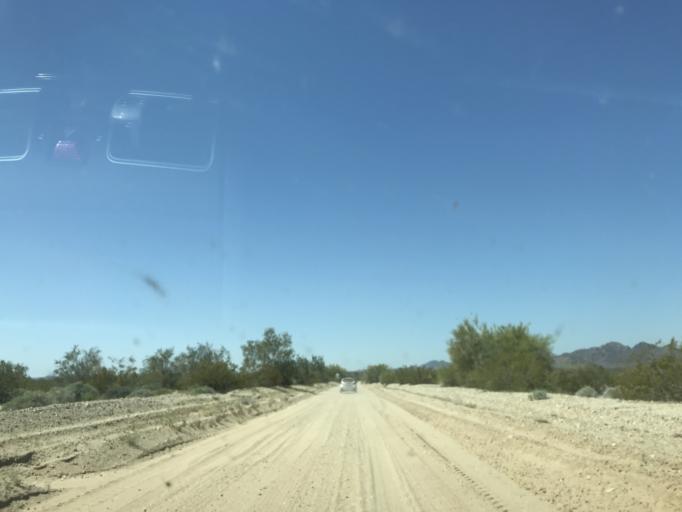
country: US
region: California
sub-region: Riverside County
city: Mesa Verde
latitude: 33.4916
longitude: -114.8857
